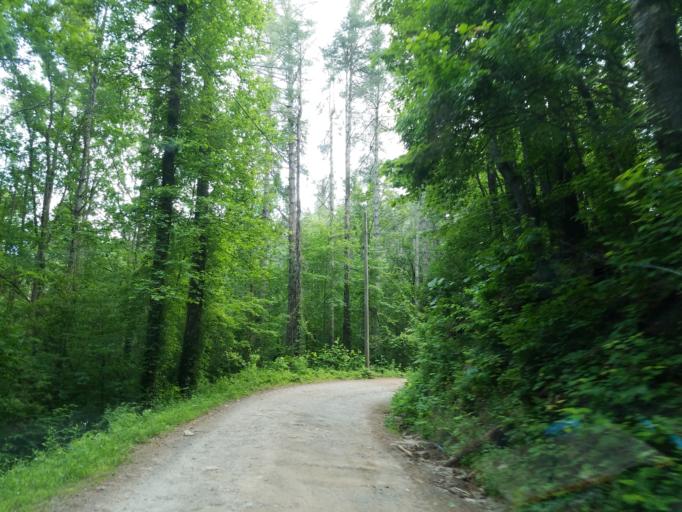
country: US
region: Georgia
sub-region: Lumpkin County
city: Dahlonega
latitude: 34.6019
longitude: -84.0942
